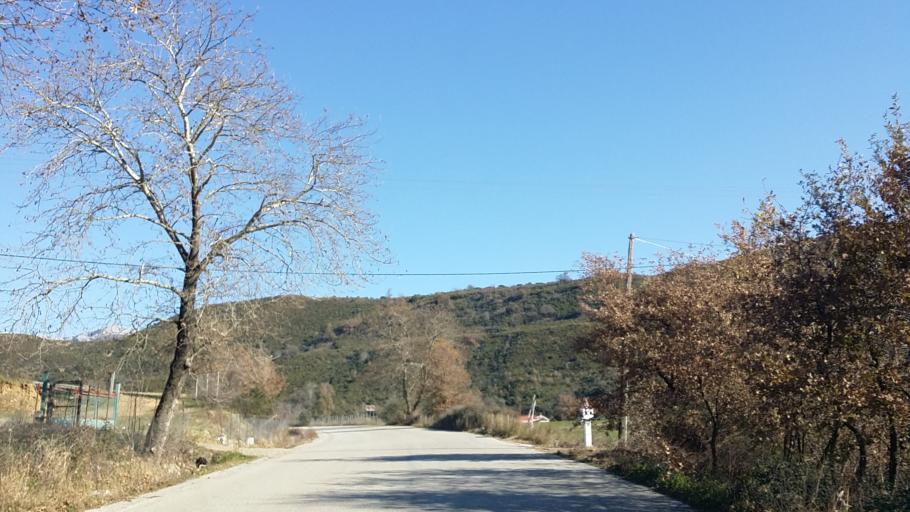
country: GR
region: West Greece
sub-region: Nomos Aitolias kai Akarnanias
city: Sardinia
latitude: 38.9102
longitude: 21.3526
